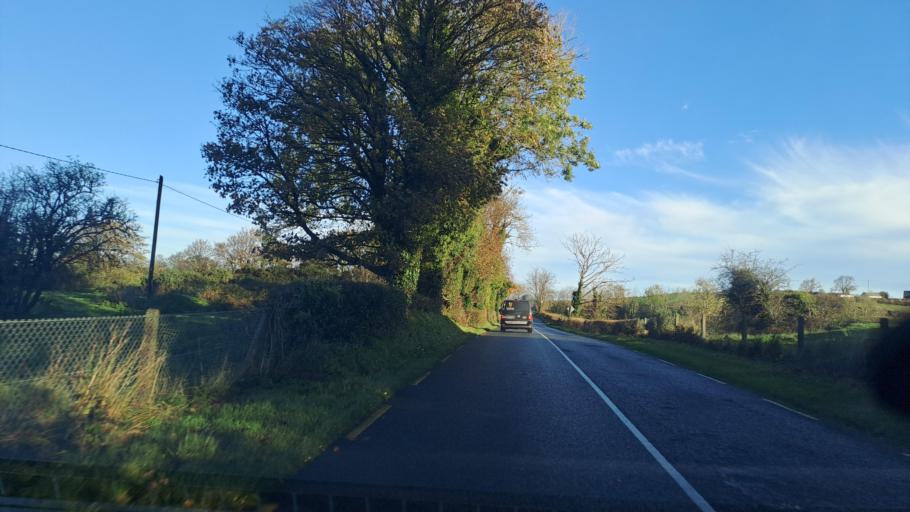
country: IE
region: Ulster
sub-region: County Monaghan
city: Monaghan
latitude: 54.1769
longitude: -6.9962
